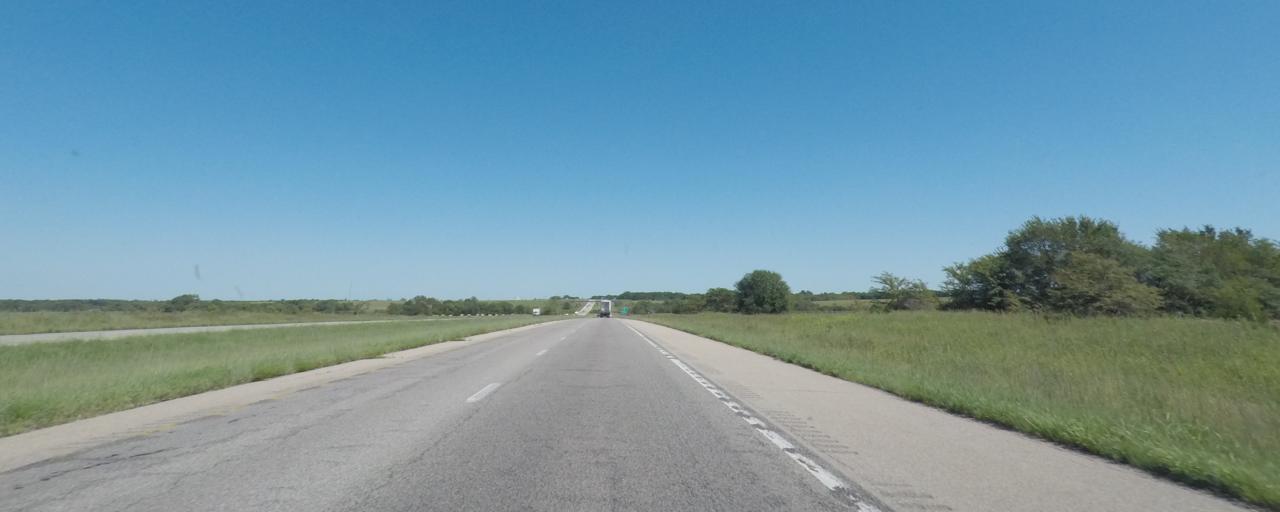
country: US
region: Kansas
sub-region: Osage County
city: Lyndon
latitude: 38.4265
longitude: -95.7603
